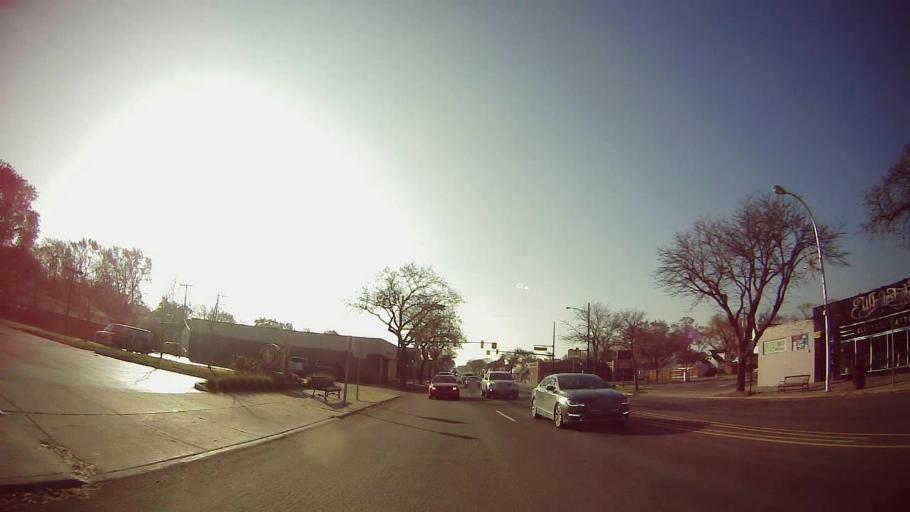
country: US
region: Michigan
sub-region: Oakland County
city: Berkley
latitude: 42.4981
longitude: -83.1837
